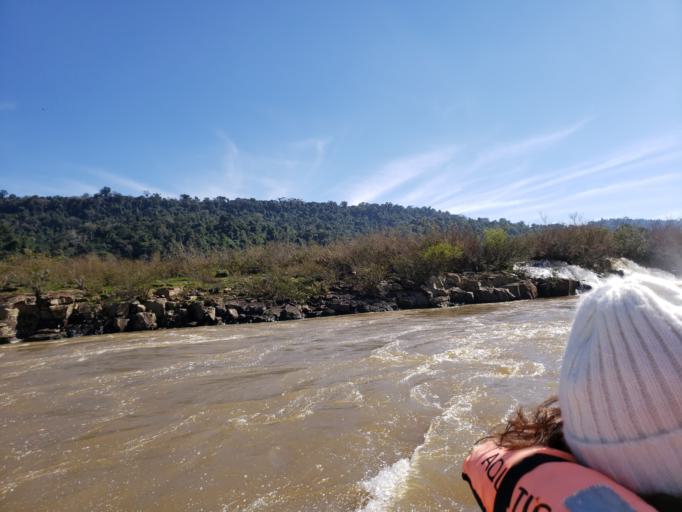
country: BR
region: Rio Grande do Sul
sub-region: Tres Passos
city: Tres Passos
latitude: -27.1507
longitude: -53.8875
